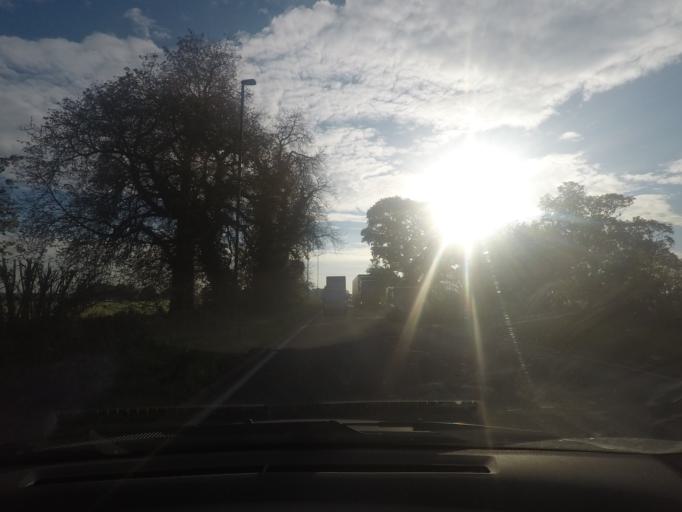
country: GB
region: England
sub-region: City of York
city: Murton
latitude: 53.9570
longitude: -0.9986
